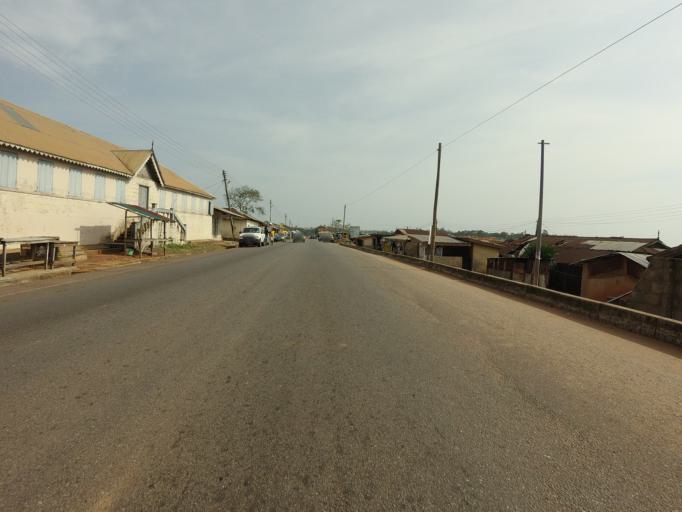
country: GH
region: Eastern
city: Aburi
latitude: 5.8906
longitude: -0.1530
